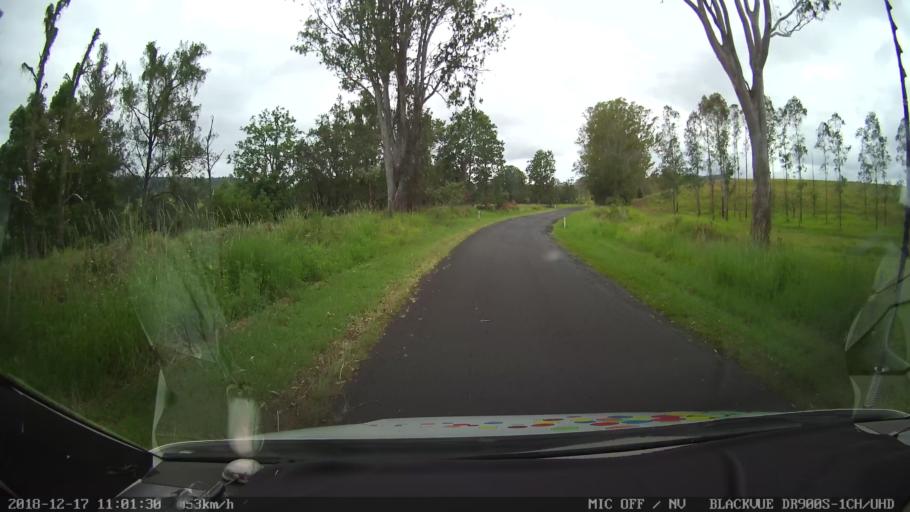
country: AU
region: New South Wales
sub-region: Richmond Valley
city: Casino
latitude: -28.8152
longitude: 152.6259
